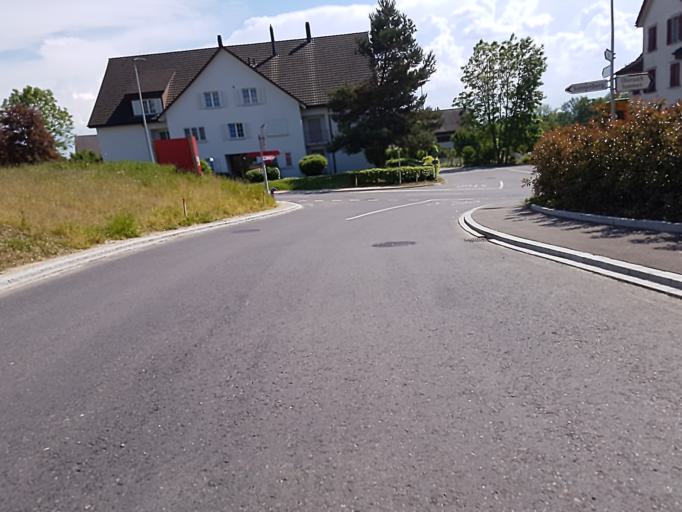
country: CH
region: Thurgau
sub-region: Arbon District
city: Amriswil
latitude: 47.5651
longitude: 9.2989
